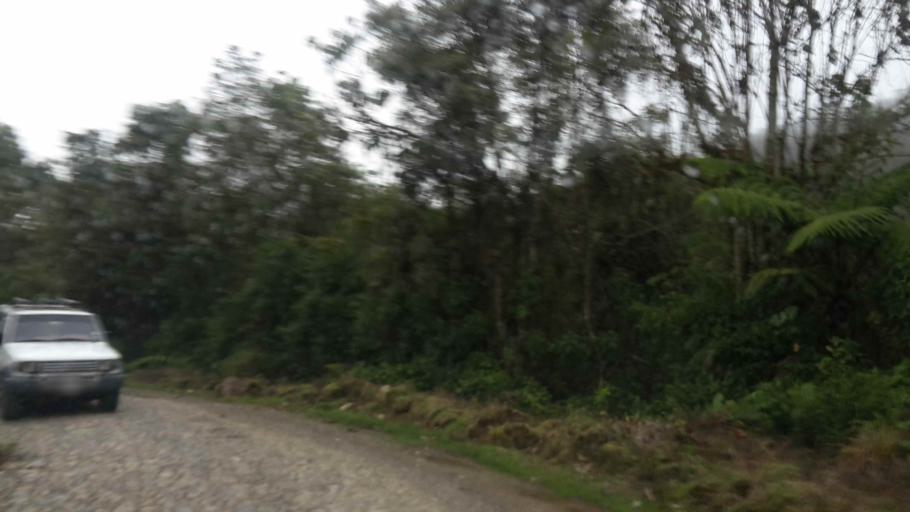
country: BO
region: Cochabamba
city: Colomi
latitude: -17.1609
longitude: -65.8993
